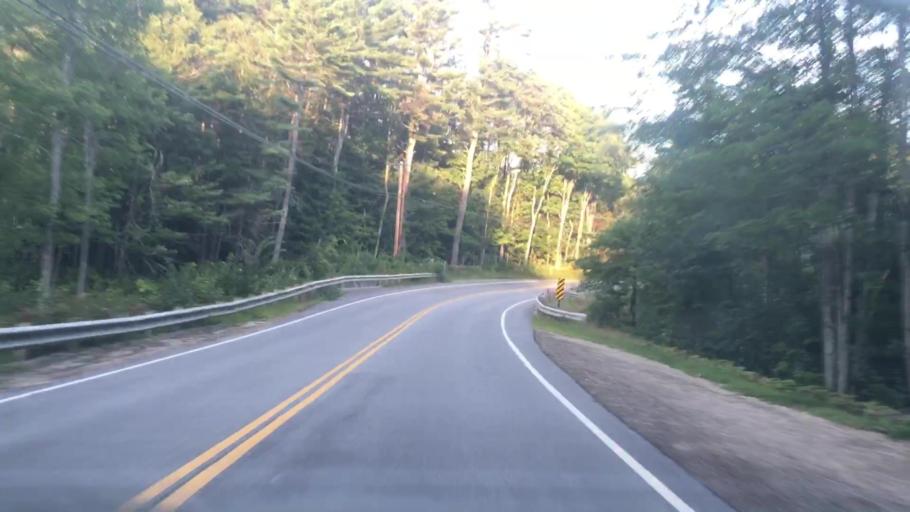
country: US
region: New Hampshire
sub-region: Belknap County
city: Barnstead
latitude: 43.4219
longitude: -71.3060
